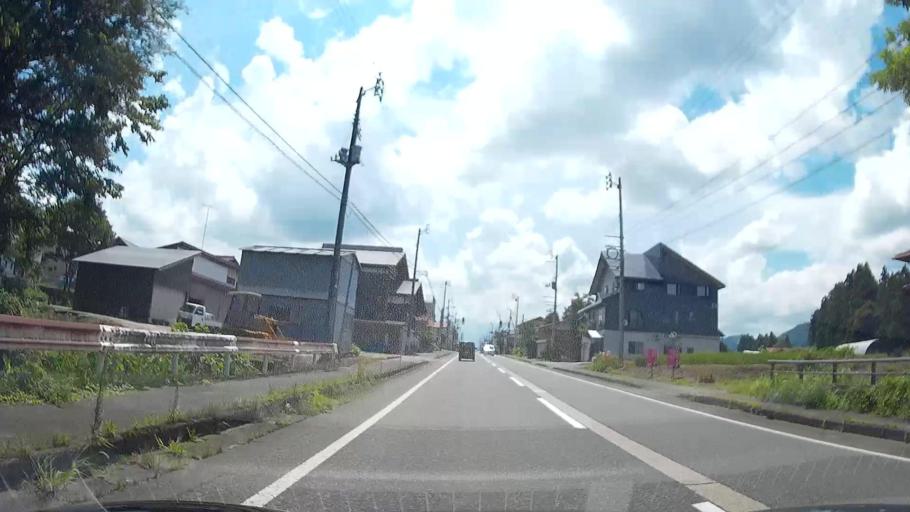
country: JP
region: Niigata
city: Tokamachi
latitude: 37.0592
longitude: 138.7054
